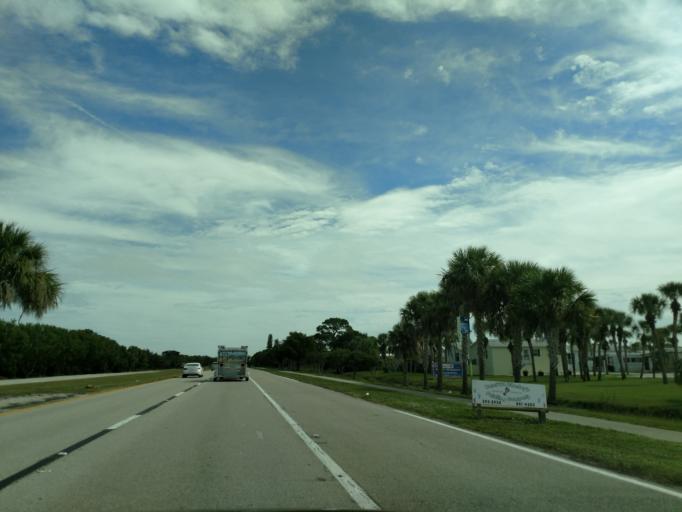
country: US
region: Florida
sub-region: Lee County
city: Iona
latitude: 26.4939
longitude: -81.9595
